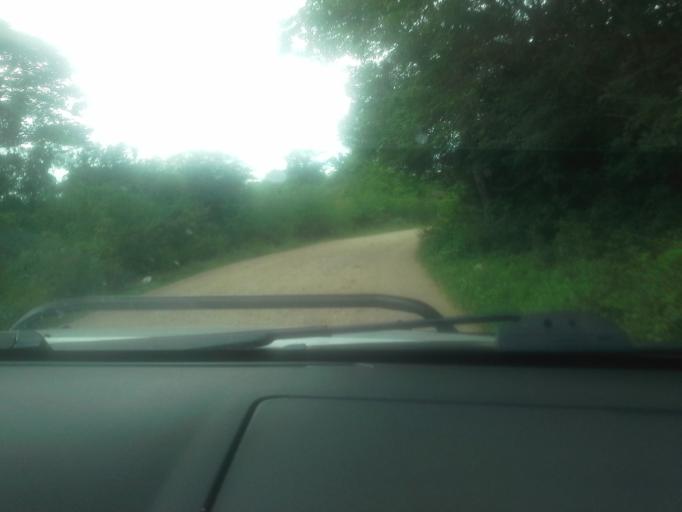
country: NI
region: Matagalpa
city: Ciudad Dario
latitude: 12.8201
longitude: -86.1933
